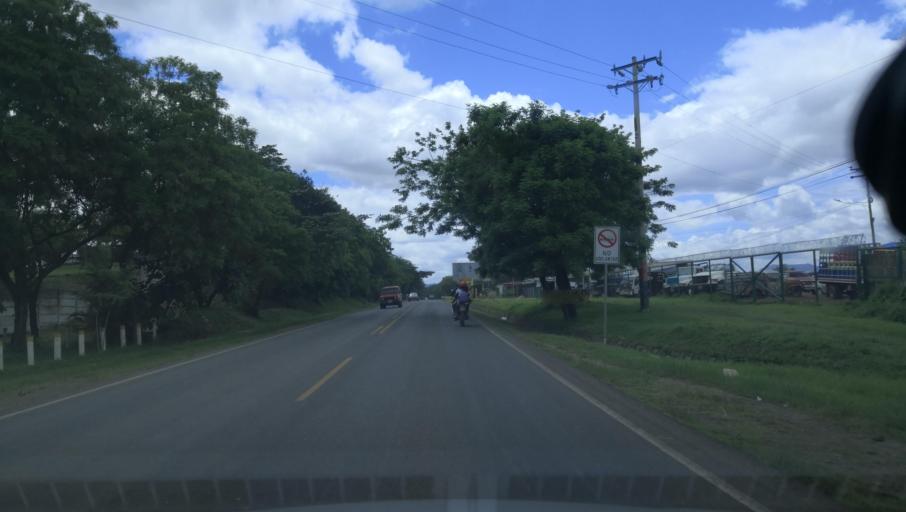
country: NI
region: Esteli
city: Esteli
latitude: 13.1217
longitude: -86.3630
